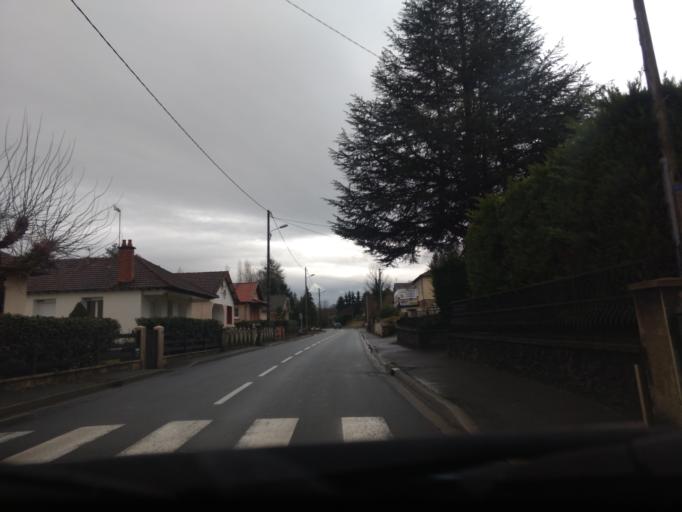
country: FR
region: Midi-Pyrenees
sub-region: Departement de l'Aveyron
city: Firmi
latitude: 44.5332
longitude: 2.3208
